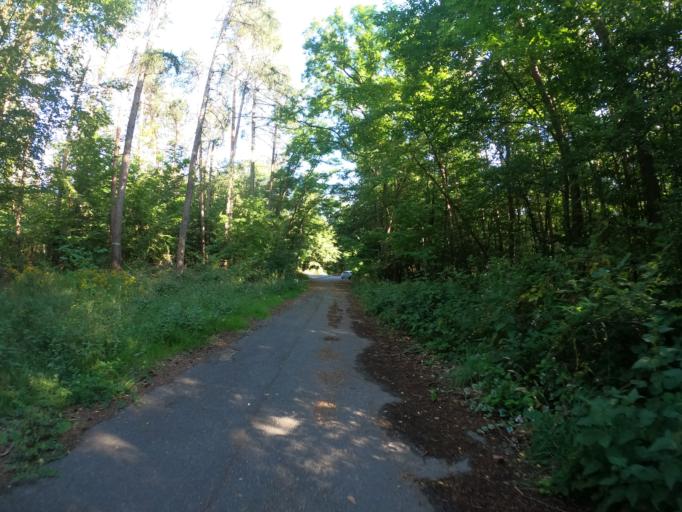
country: DE
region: Hesse
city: Morfelden-Walldorf
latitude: 49.9875
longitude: 8.6171
